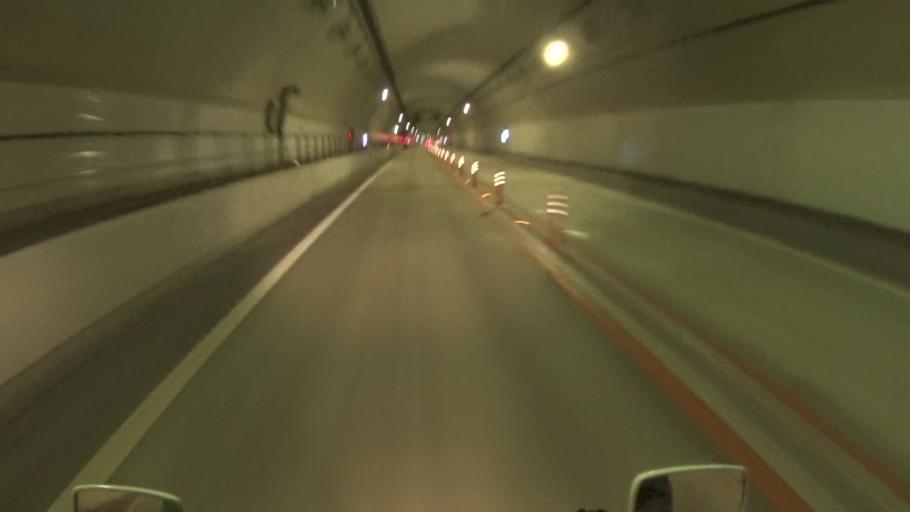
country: JP
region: Kyoto
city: Miyazu
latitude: 35.5407
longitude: 135.1570
